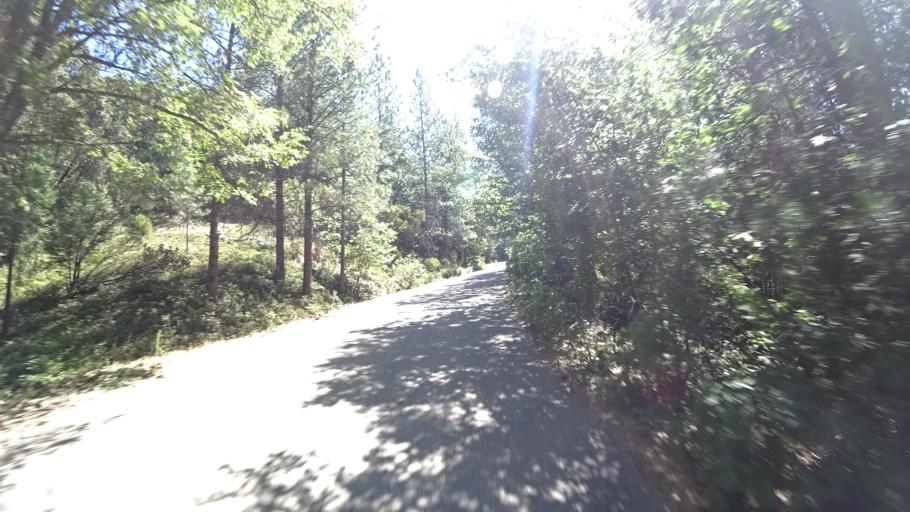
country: US
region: California
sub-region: Amador County
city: Pioneer
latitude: 38.4256
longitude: -120.4876
